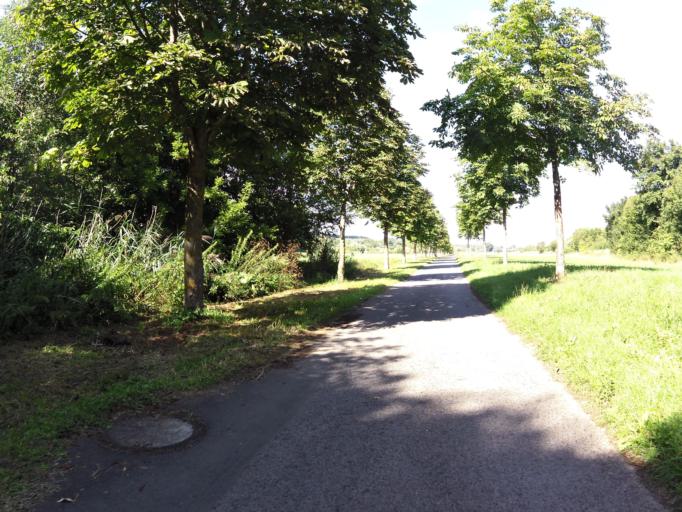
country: DE
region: Bavaria
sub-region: Regierungsbezirk Unterfranken
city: Marktsteft
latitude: 49.7009
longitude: 10.1341
